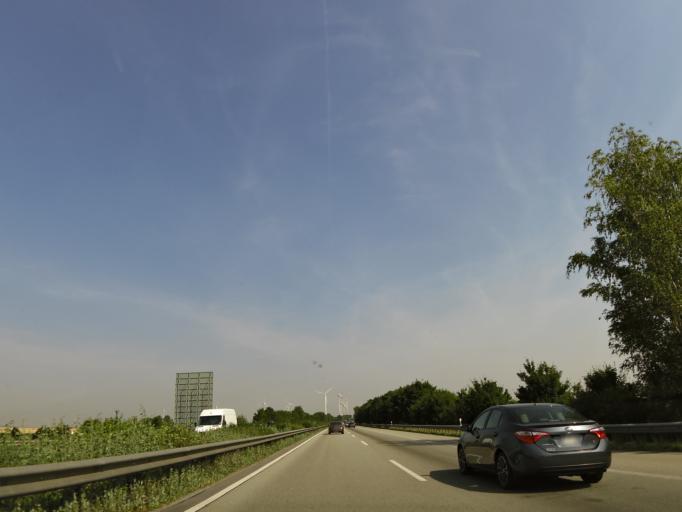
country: DE
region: Rheinland-Pfalz
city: Grossniedesheim
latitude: 49.5668
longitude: 8.3038
